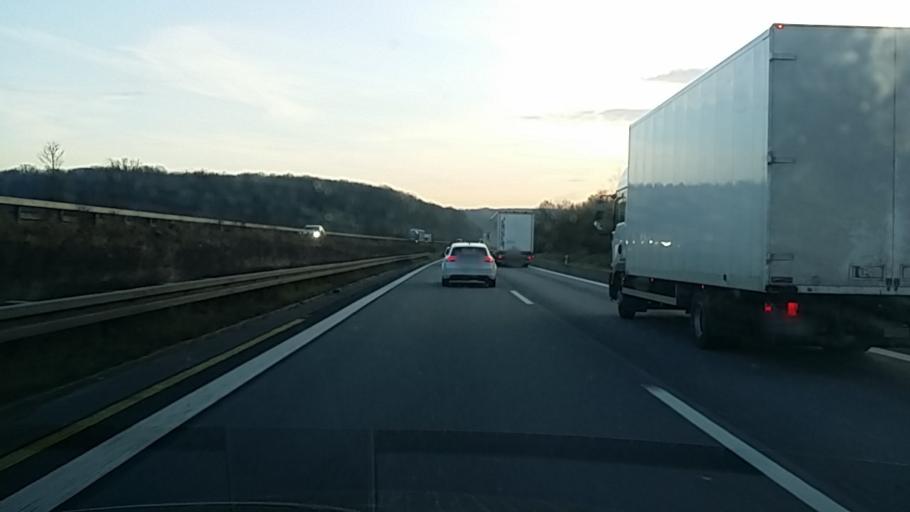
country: DE
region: Bavaria
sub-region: Regierungsbezirk Unterfranken
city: Werneck
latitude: 50.0256
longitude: 10.0698
